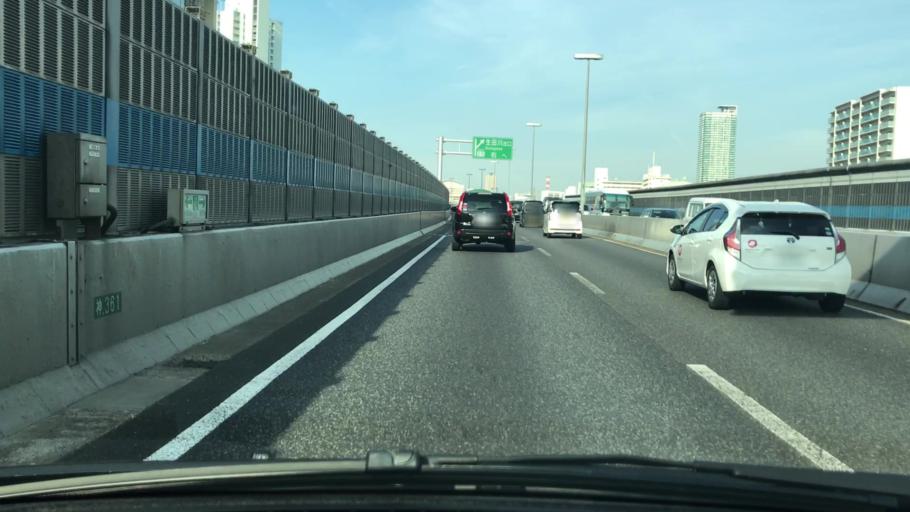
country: JP
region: Hyogo
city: Kobe
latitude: 34.6995
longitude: 135.2121
